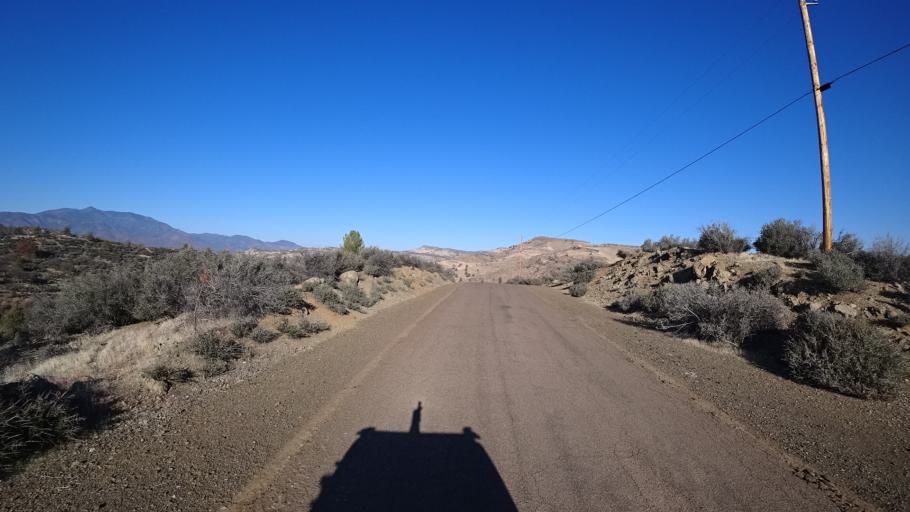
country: US
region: California
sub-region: Siskiyou County
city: Montague
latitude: 41.8939
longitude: -122.4858
